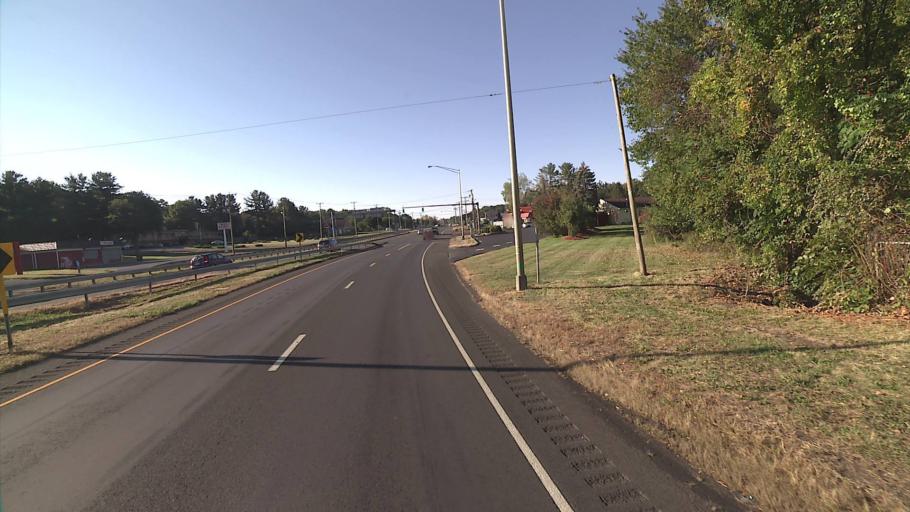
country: US
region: Connecticut
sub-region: Hartford County
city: Newington
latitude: 41.7092
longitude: -72.7003
